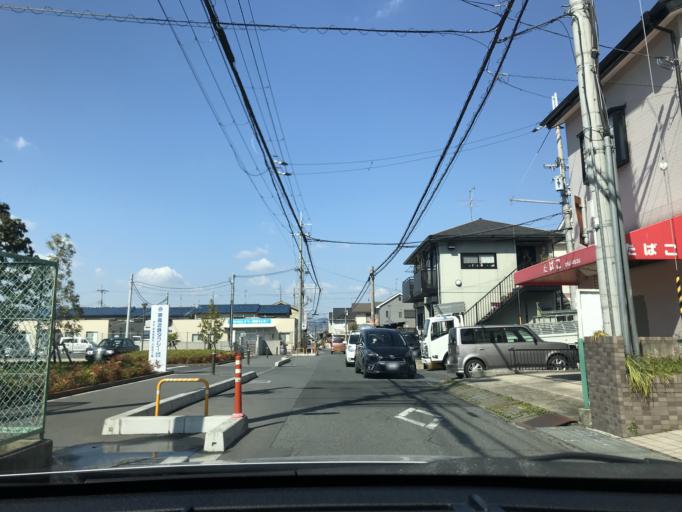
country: JP
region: Nara
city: Nara-shi
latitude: 34.6700
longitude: 135.8175
